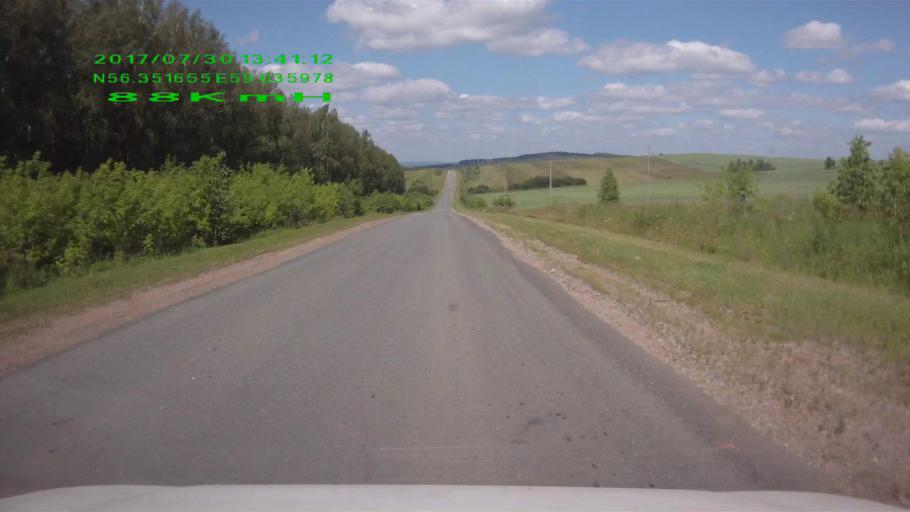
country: RU
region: Sverdlovsk
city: Mikhaylovsk
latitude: 56.3521
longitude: 59.0360
